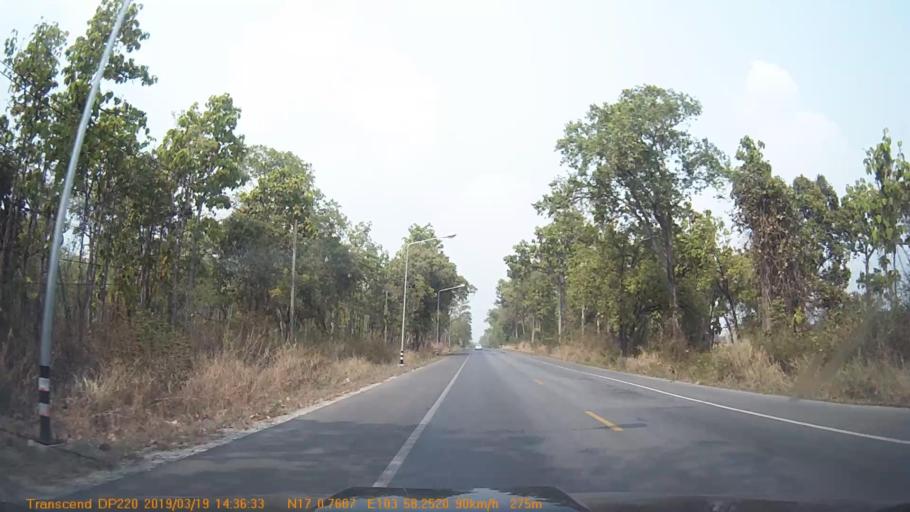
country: TH
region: Sakon Nakhon
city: Phu Phan
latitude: 17.0129
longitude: 103.9710
